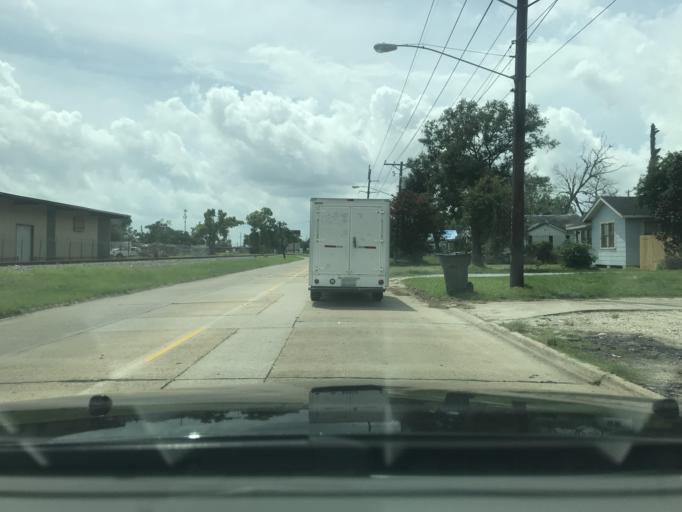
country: US
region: Louisiana
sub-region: Calcasieu Parish
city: Lake Charles
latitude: 30.2133
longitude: -93.2061
